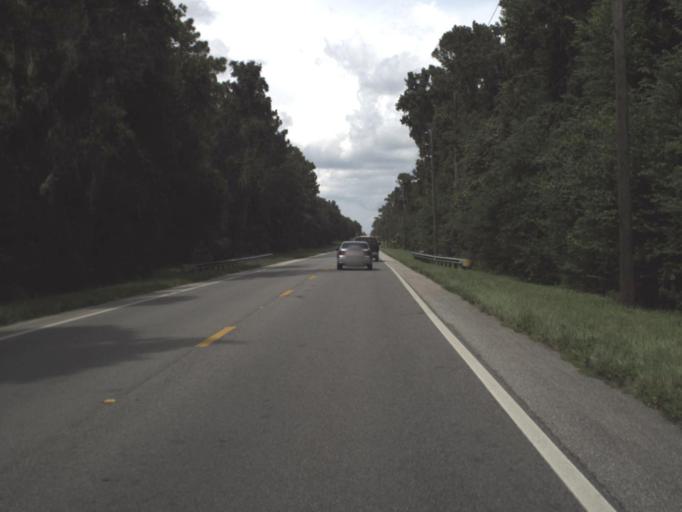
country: US
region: Florida
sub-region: Hernando County
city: Brooksville
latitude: 28.6021
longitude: -82.3643
